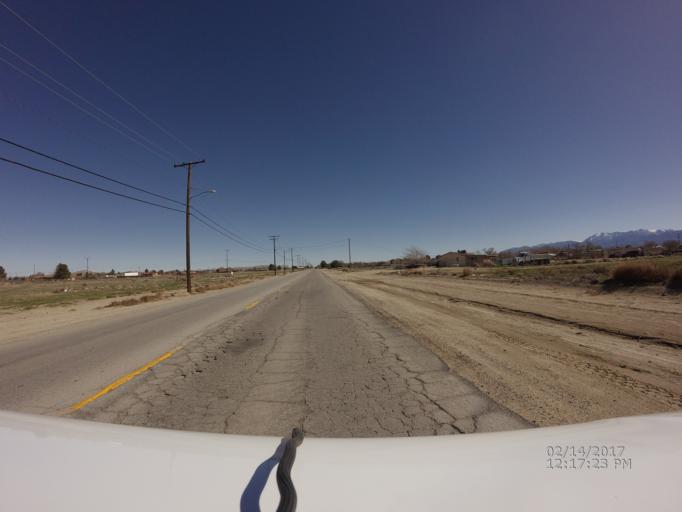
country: US
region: California
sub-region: Los Angeles County
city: Littlerock
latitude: 34.5797
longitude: -117.9663
